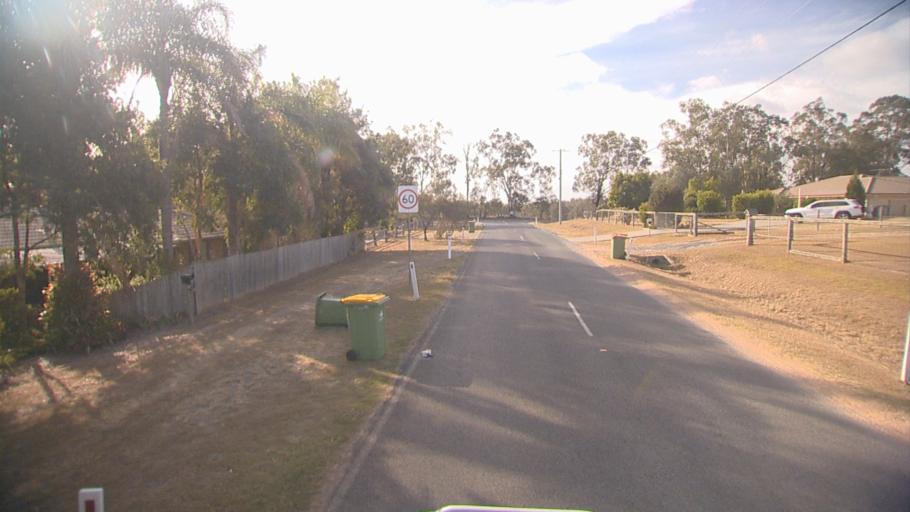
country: AU
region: Queensland
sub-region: Logan
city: Cedar Vale
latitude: -27.8658
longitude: 153.0056
